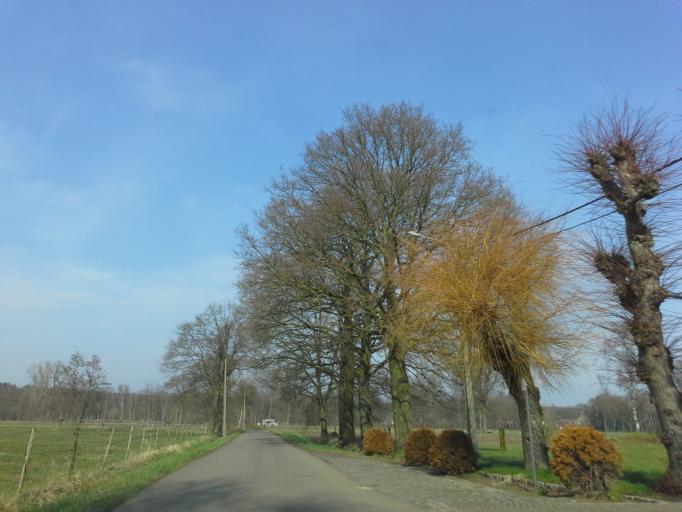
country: BE
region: Flanders
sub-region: Provincie Antwerpen
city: Meerhout
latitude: 51.1345
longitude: 5.0579
